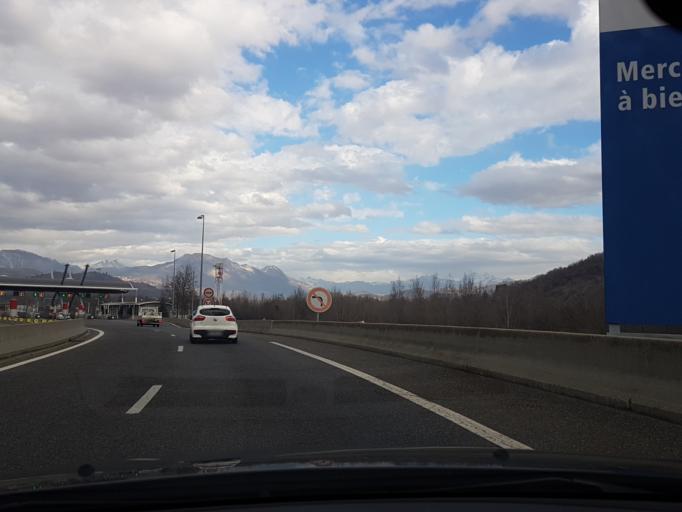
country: FR
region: Provence-Alpes-Cote d'Azur
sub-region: Departement des Hautes-Alpes
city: Tallard
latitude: 44.4389
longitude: 6.0297
